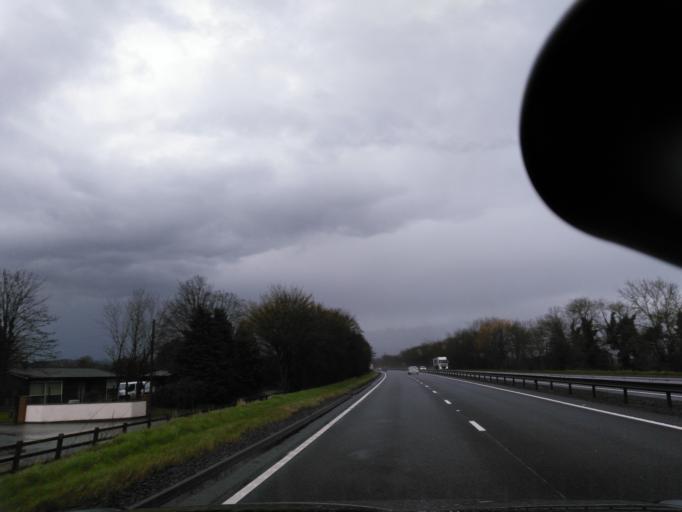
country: GB
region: England
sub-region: North Yorkshire
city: Thirsk
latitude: 54.2167
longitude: -1.3379
